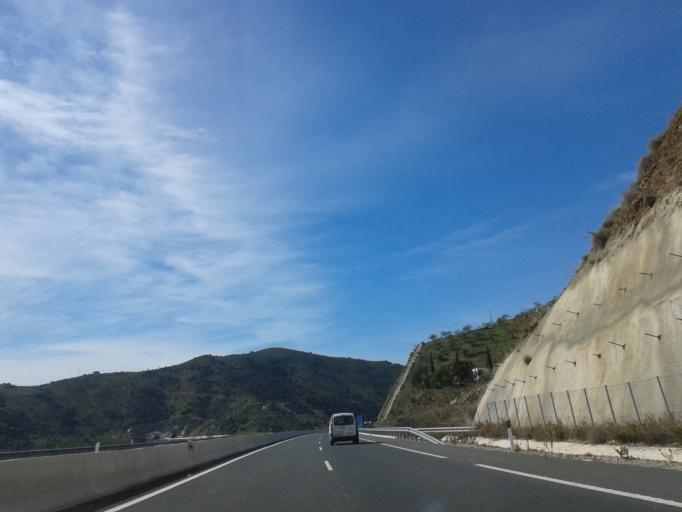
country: ES
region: Andalusia
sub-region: Provincia de Malaga
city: Casabermeja
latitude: 36.8830
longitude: -4.4738
